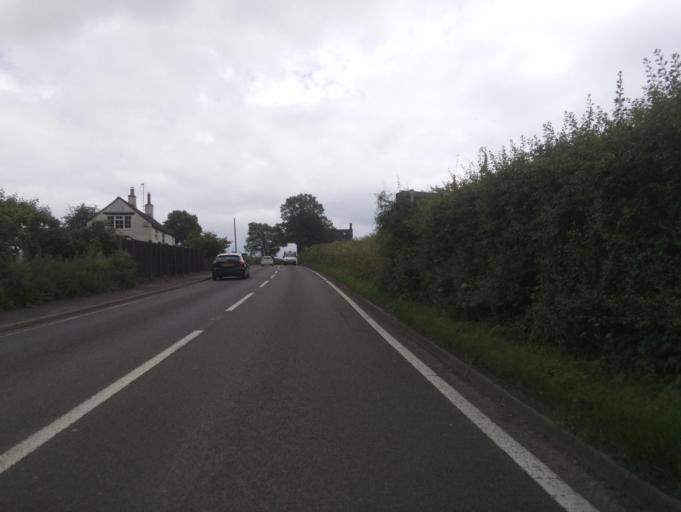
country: GB
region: England
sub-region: Derbyshire
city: Ashbourne
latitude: 53.0025
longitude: -1.7107
